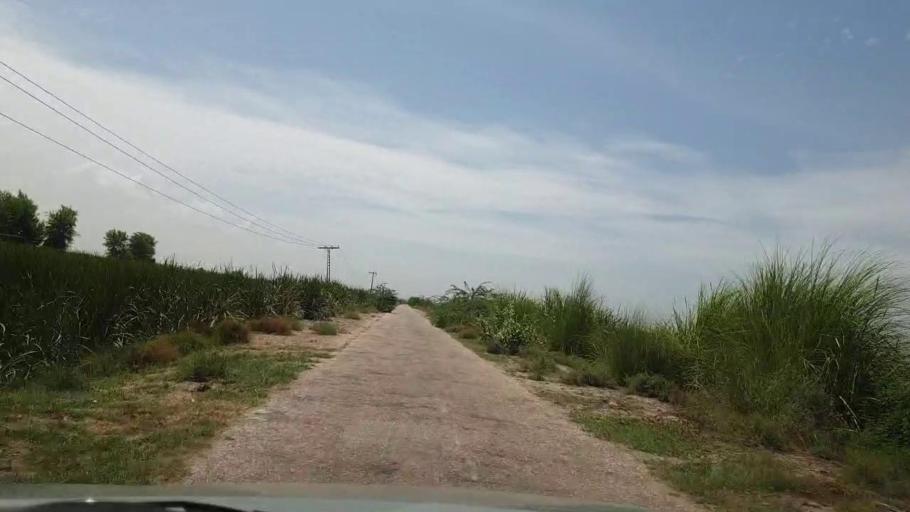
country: PK
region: Sindh
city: Bozdar
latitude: 27.0649
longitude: 68.9825
